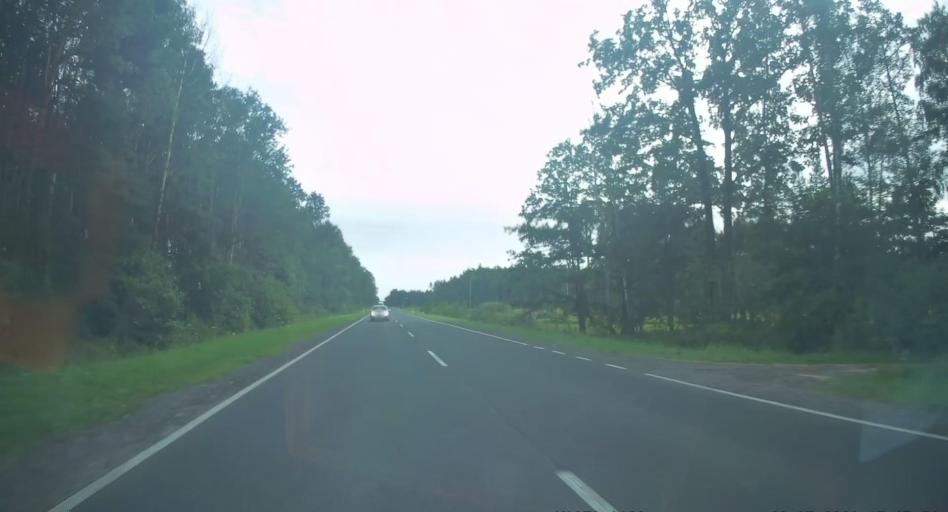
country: PL
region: Lodz Voivodeship
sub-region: Powiat radomszczanski
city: Plawno
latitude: 50.9793
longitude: 19.4106
